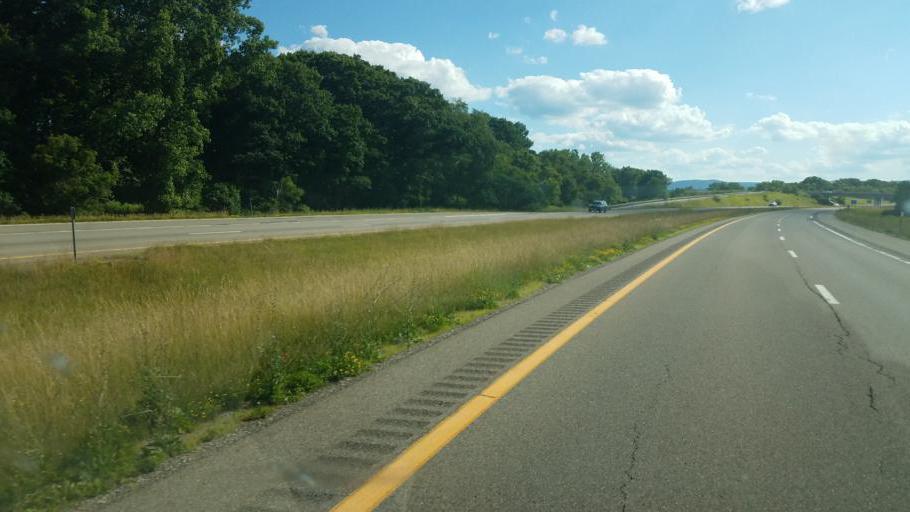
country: US
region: New York
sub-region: Cattaraugus County
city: Olean
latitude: 42.1032
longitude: -78.4241
